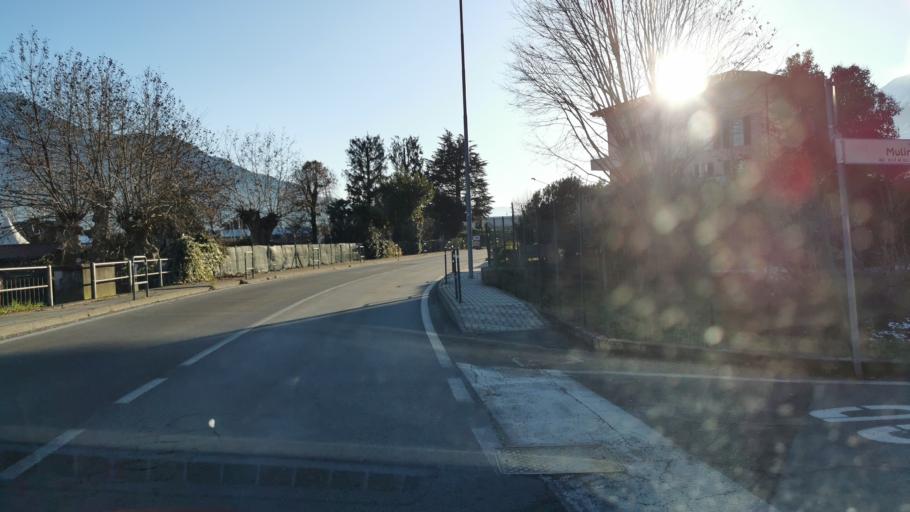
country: IT
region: Lombardy
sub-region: Provincia di Como
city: Vercana
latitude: 46.1562
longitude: 9.3380
